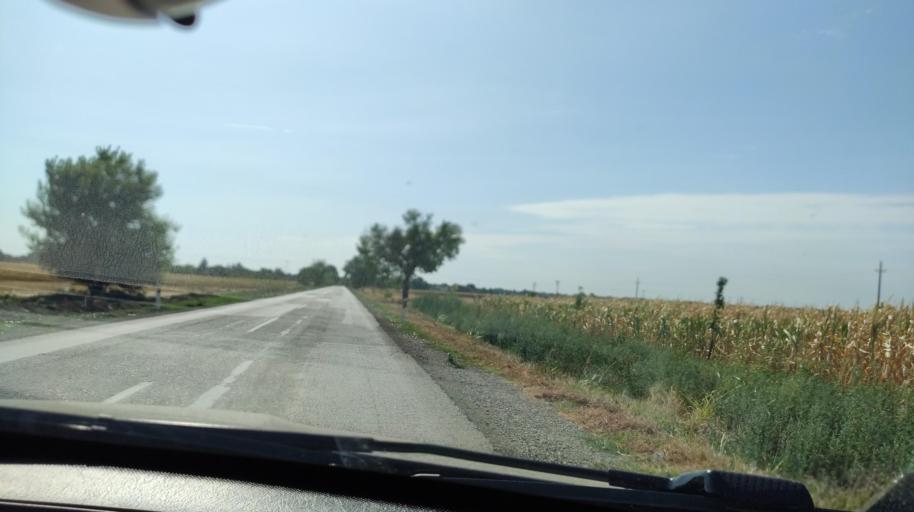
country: RS
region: Autonomna Pokrajina Vojvodina
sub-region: Severnobacki Okrug
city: Backa Topola
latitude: 45.8199
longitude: 19.6101
